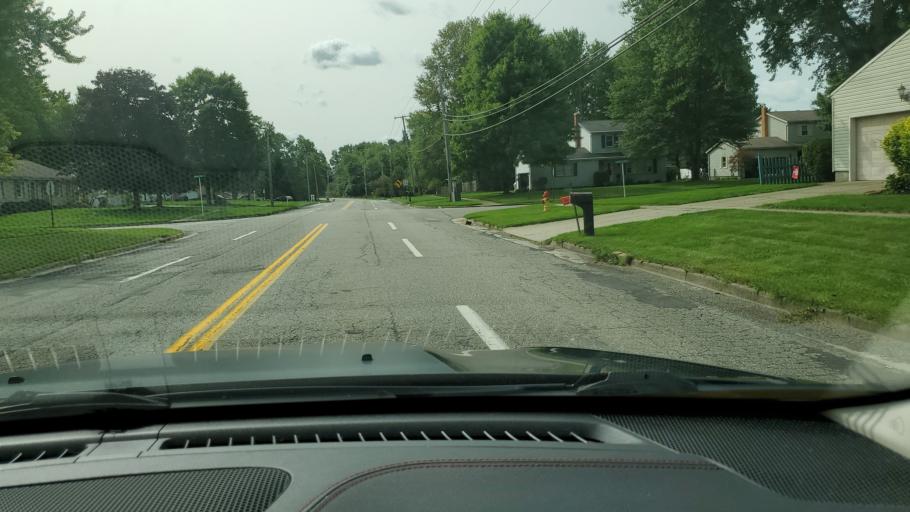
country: US
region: Ohio
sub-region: Mahoning County
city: Boardman
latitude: 40.9955
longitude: -80.6723
